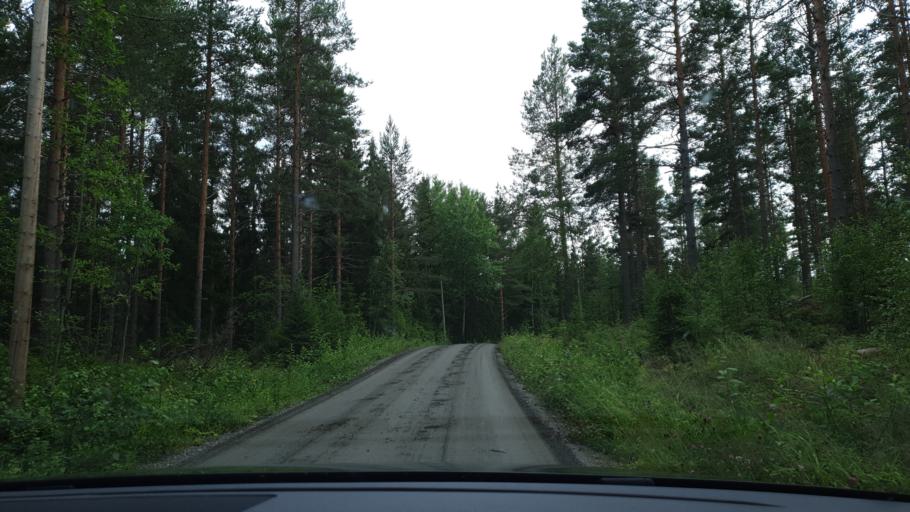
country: SE
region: Gaevleborg
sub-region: Hudiksvalls Kommun
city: Iggesund
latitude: 61.5083
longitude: 17.0187
